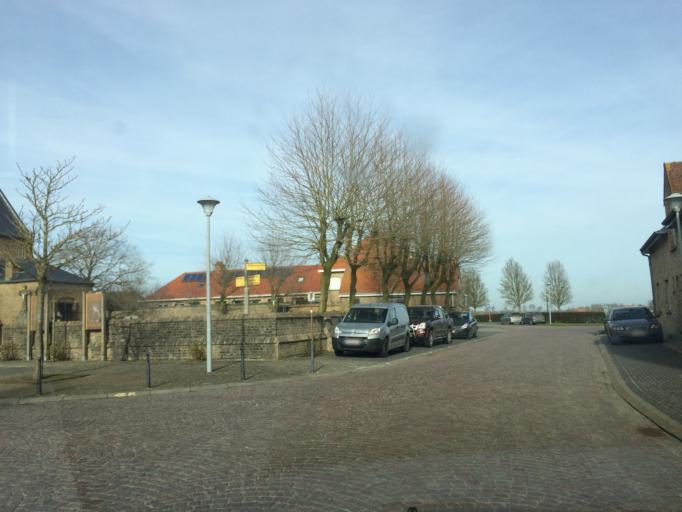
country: BE
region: Flanders
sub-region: Provincie West-Vlaanderen
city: Diksmuide
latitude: 51.0767
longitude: 2.8250
